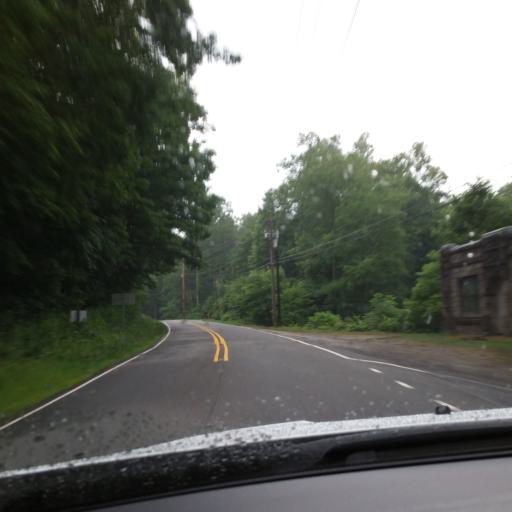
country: US
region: North Carolina
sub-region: Yancey County
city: Burnsville
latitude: 35.7702
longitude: -82.1973
